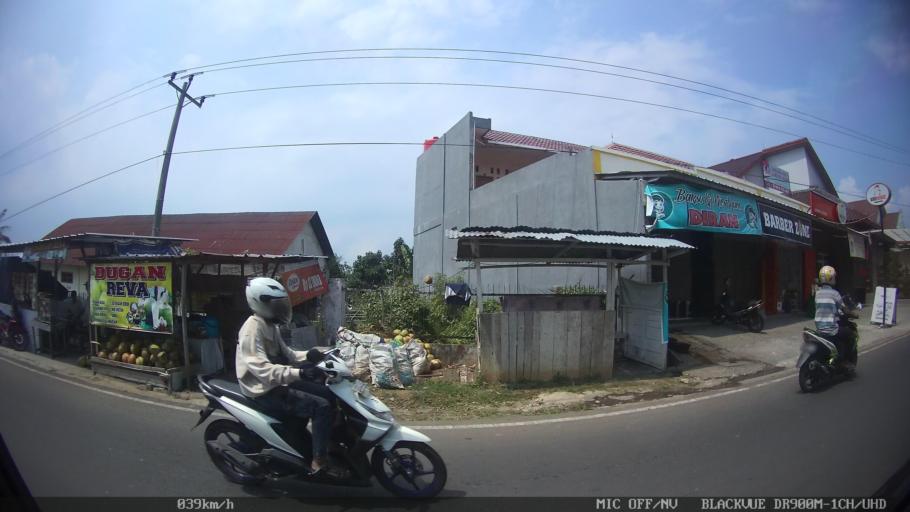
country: ID
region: Lampung
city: Bandarlampung
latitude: -5.4394
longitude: 105.2627
